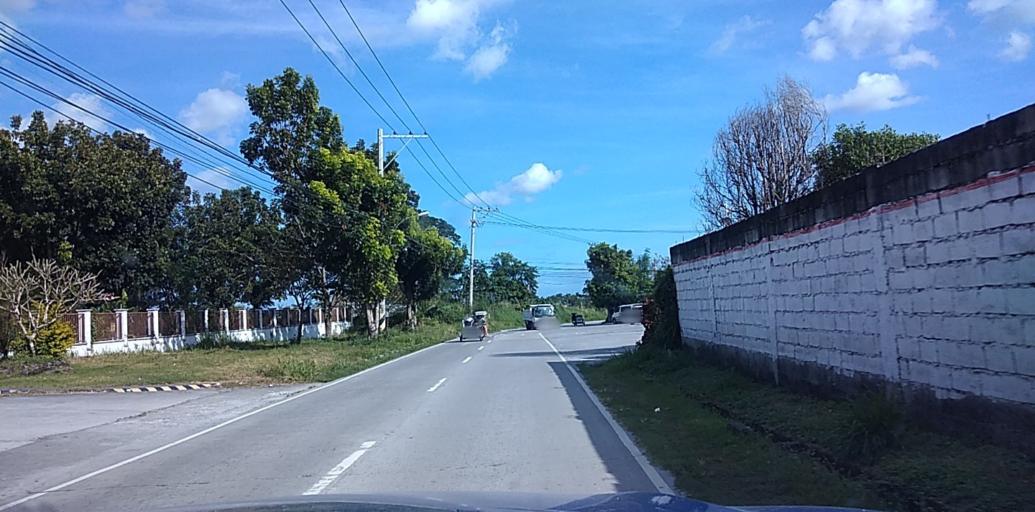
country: PH
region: Central Luzon
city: Santol
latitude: 15.1452
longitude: 120.5543
